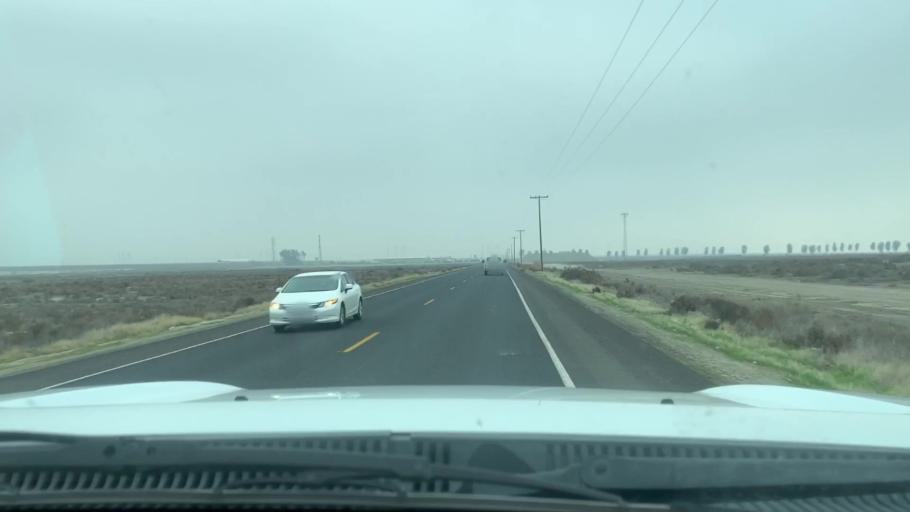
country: US
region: California
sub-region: Kern County
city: Buttonwillow
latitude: 35.4995
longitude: -119.5578
